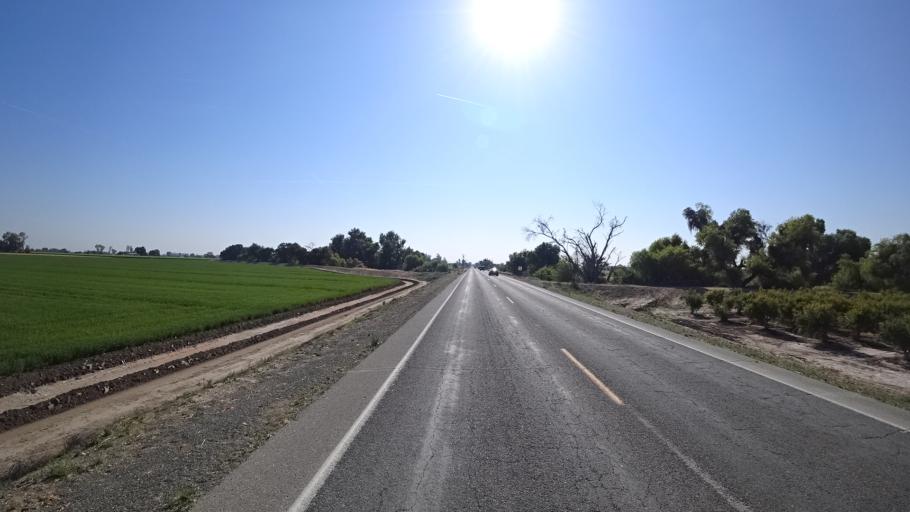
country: US
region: California
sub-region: Fresno County
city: Riverdale
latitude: 36.3439
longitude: -119.8638
